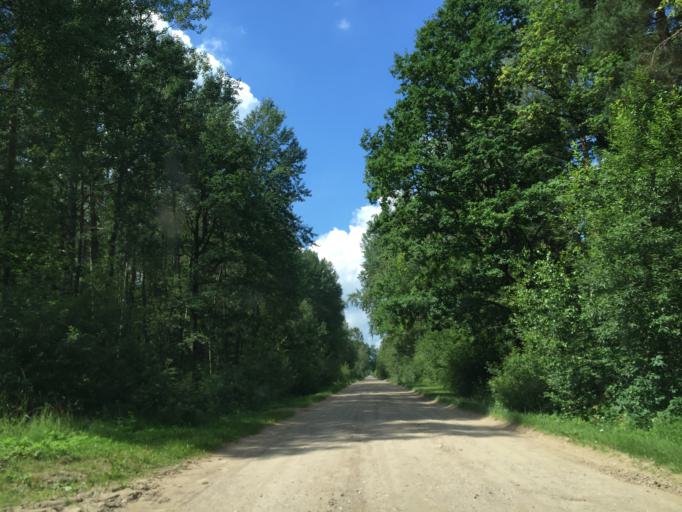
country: LV
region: Ozolnieku
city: Ozolnieki
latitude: 56.6864
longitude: 23.7523
